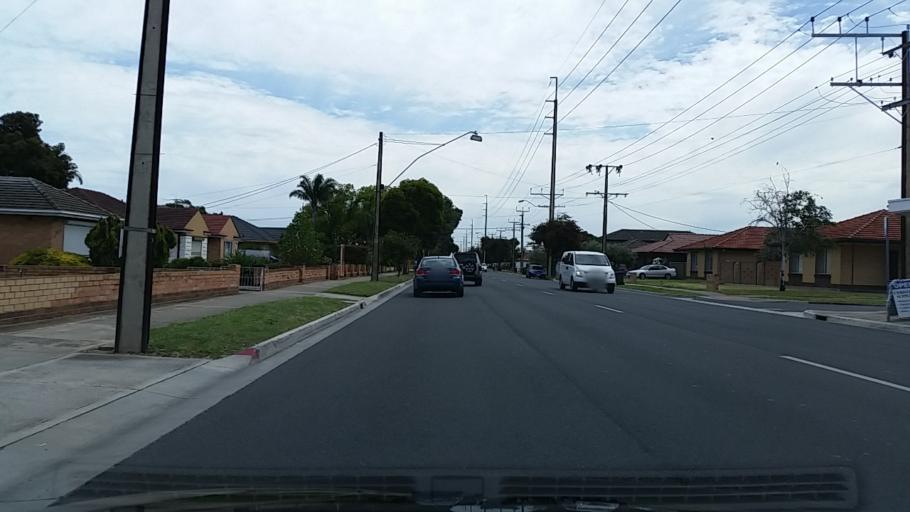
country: AU
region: South Australia
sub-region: Charles Sturt
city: Findon
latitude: -34.8998
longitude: 138.5321
